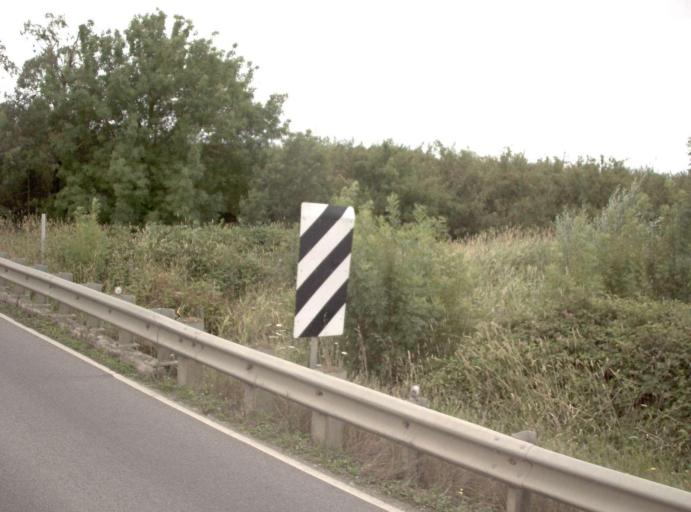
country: AU
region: Victoria
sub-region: Yarra Ranges
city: Yarra Glen
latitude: -37.6937
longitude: 145.3841
